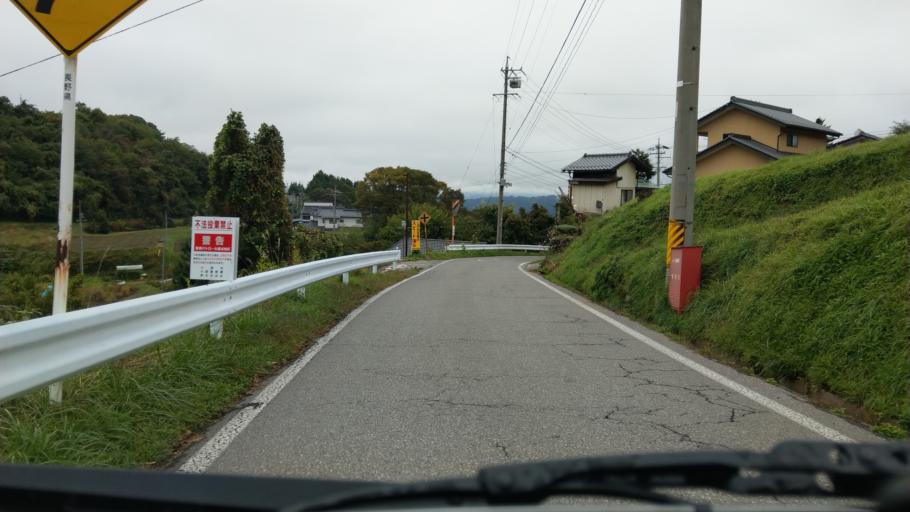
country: JP
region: Nagano
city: Komoro
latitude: 36.3511
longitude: 138.4324
